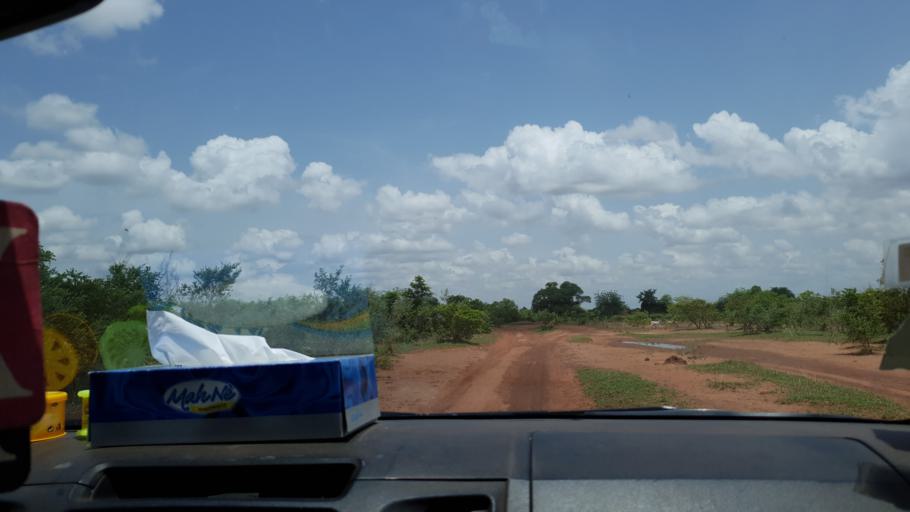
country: ML
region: Koulikoro
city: Banamba
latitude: 13.3783
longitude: -7.2120
